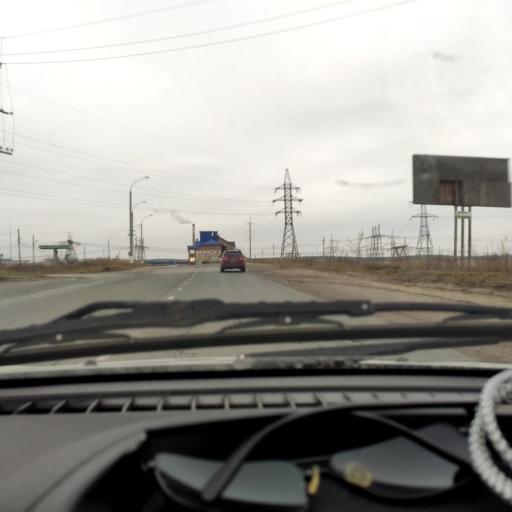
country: RU
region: Samara
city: Zhigulevsk
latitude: 53.4830
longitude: 49.5109
